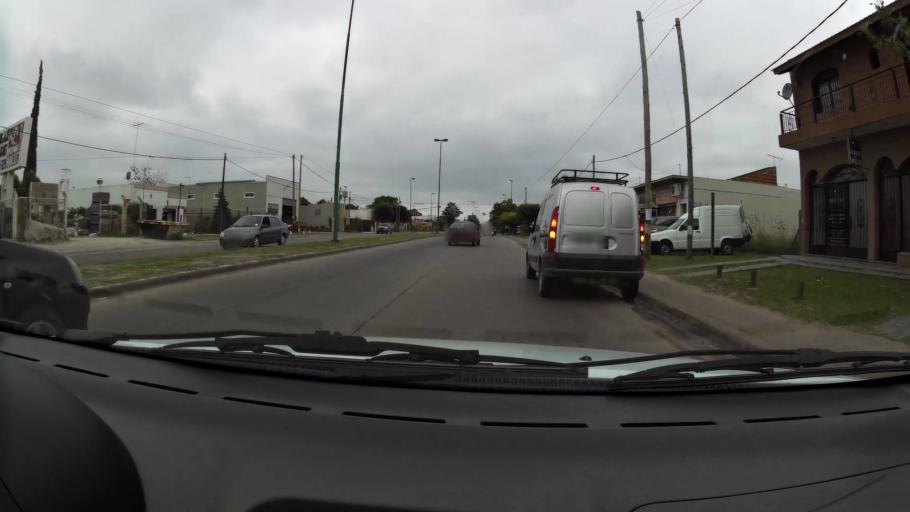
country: AR
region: Buenos Aires
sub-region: Partido de La Plata
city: La Plata
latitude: -34.9849
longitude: -58.0367
